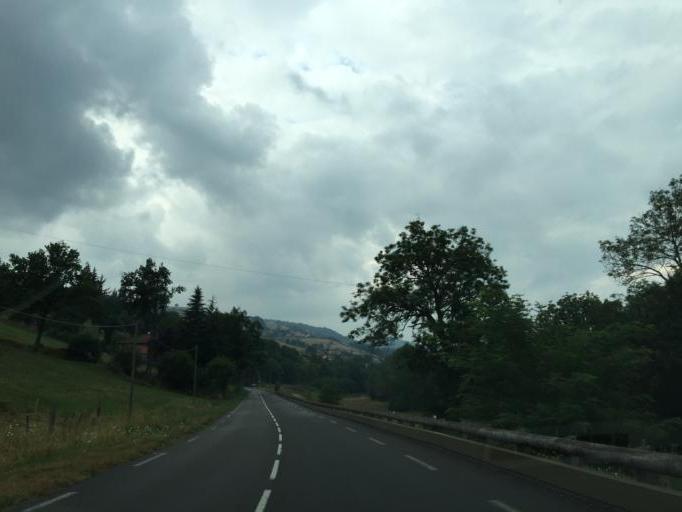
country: FR
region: Rhone-Alpes
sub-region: Departement de la Loire
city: Sorbiers
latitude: 45.5124
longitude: 4.4420
